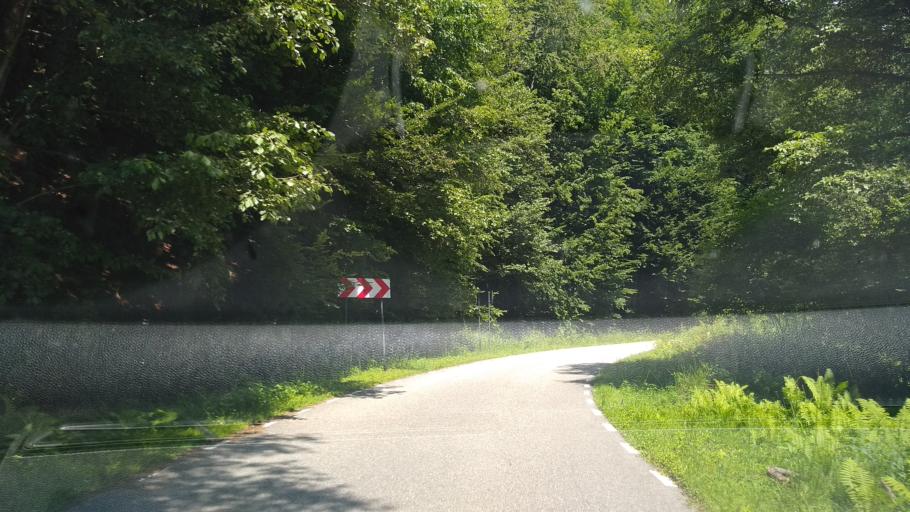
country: RO
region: Hunedoara
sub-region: Comuna Orastioara de Sus
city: Orastioara de Sus
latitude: 45.6218
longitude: 23.2707
